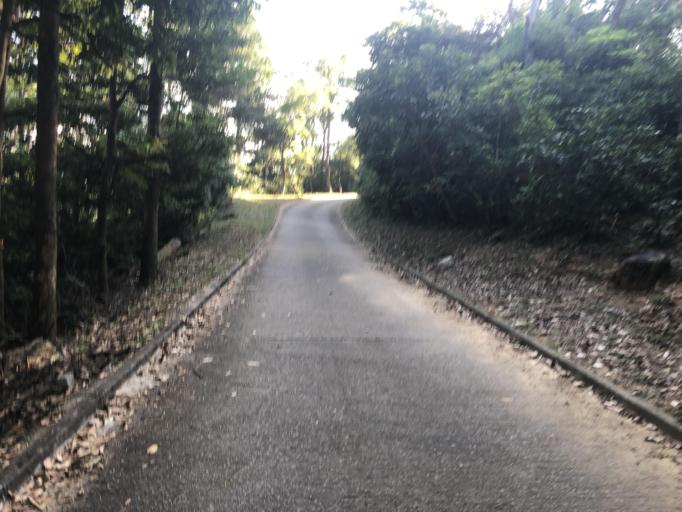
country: HK
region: Tsuen Wan
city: Tsuen Wan
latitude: 22.3992
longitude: 114.0825
